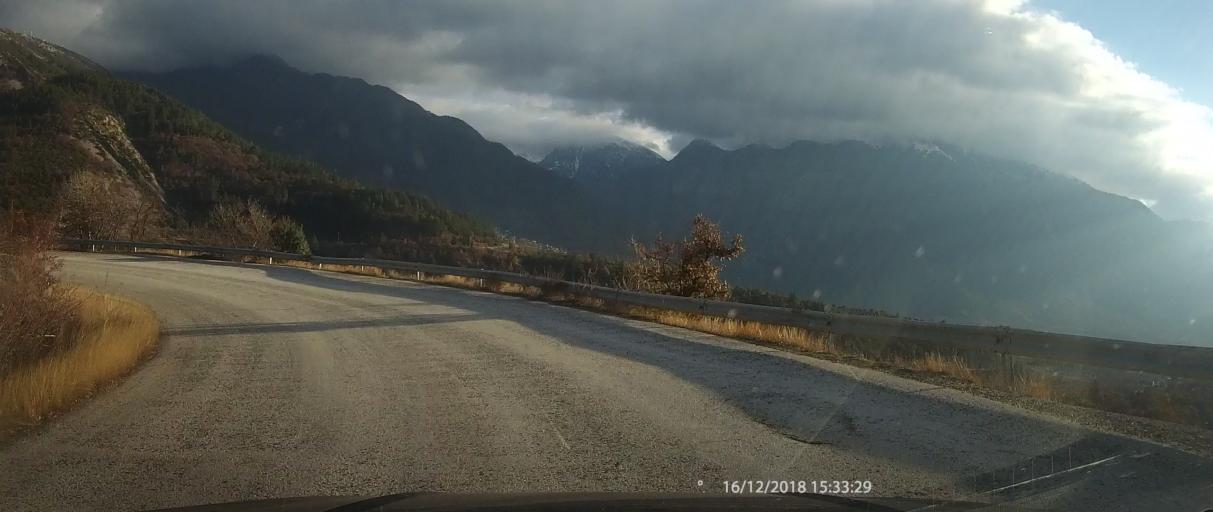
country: GR
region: Epirus
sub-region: Nomos Ioanninon
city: Konitsa
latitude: 40.0624
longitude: 20.7363
